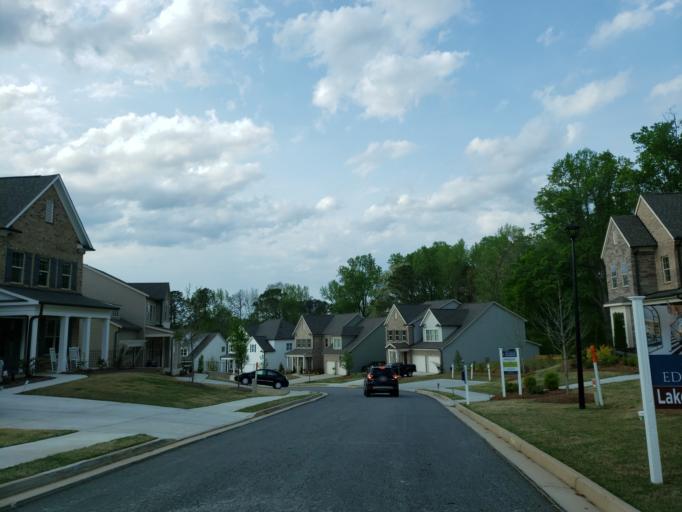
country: US
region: Georgia
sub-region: Cherokee County
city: Holly Springs
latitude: 34.1680
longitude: -84.4313
